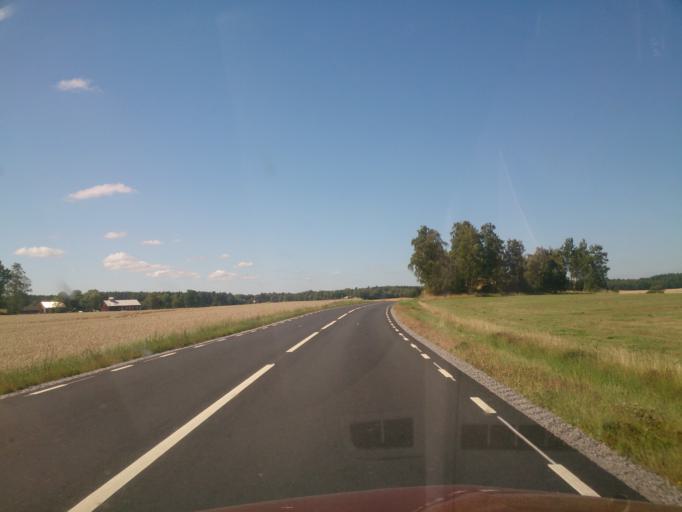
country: SE
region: OEstergoetland
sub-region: Norrkopings Kommun
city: Krokek
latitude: 58.5750
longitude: 16.4664
